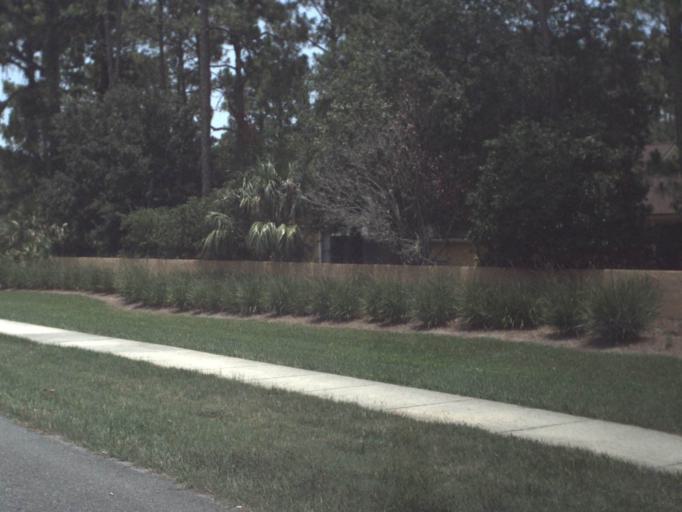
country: US
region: Florida
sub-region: Saint Johns County
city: Sawgrass
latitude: 30.2122
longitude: -81.3805
